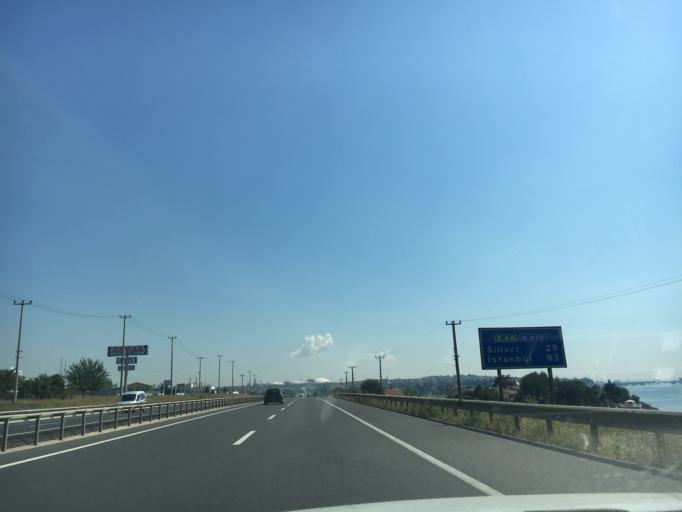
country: TR
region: Tekirdag
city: Marmara Ereglisi
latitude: 40.9800
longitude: 27.9581
